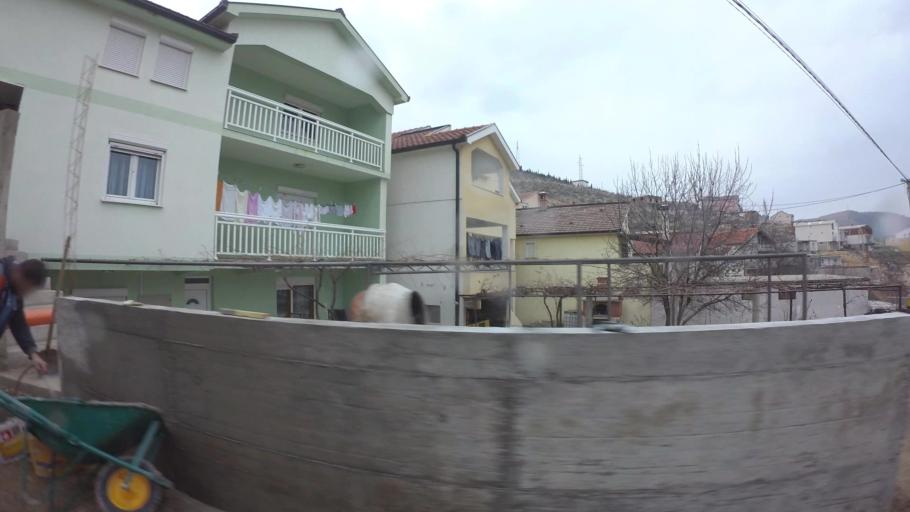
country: BA
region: Federation of Bosnia and Herzegovina
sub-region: Hercegovacko-Bosanski Kanton
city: Mostar
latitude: 43.3574
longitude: 17.8180
